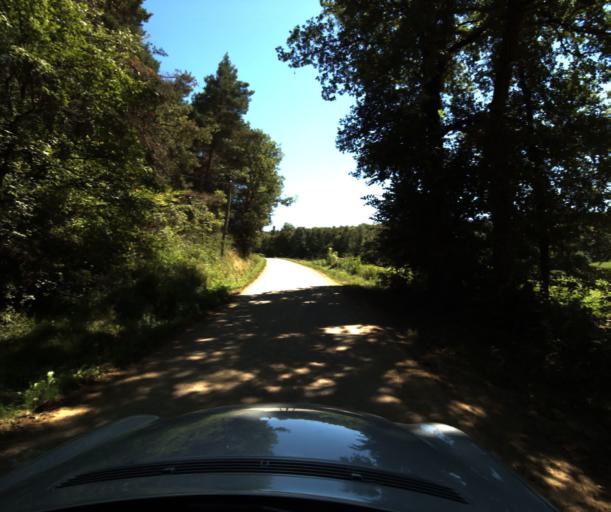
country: FR
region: Midi-Pyrenees
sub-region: Departement de l'Ariege
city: Belesta
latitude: 42.9749
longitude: 1.9096
